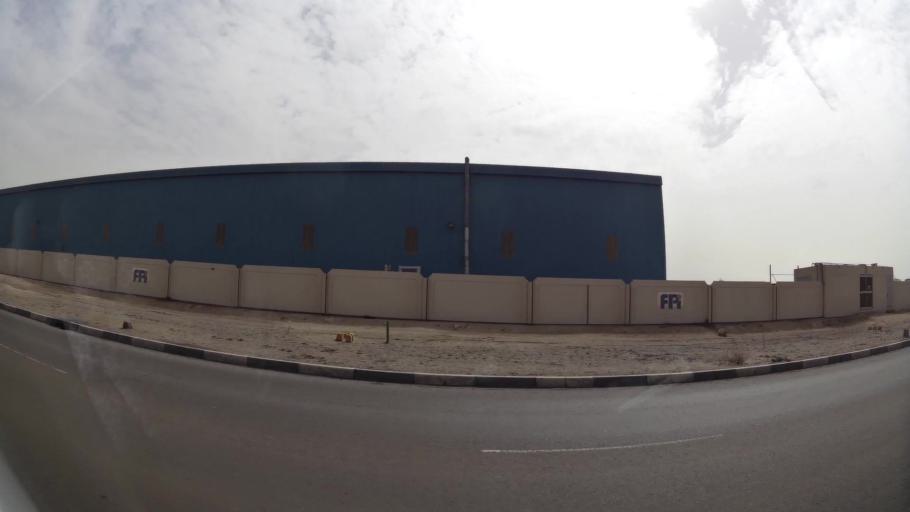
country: AE
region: Abu Dhabi
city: Abu Dhabi
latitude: 24.3227
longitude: 54.4915
